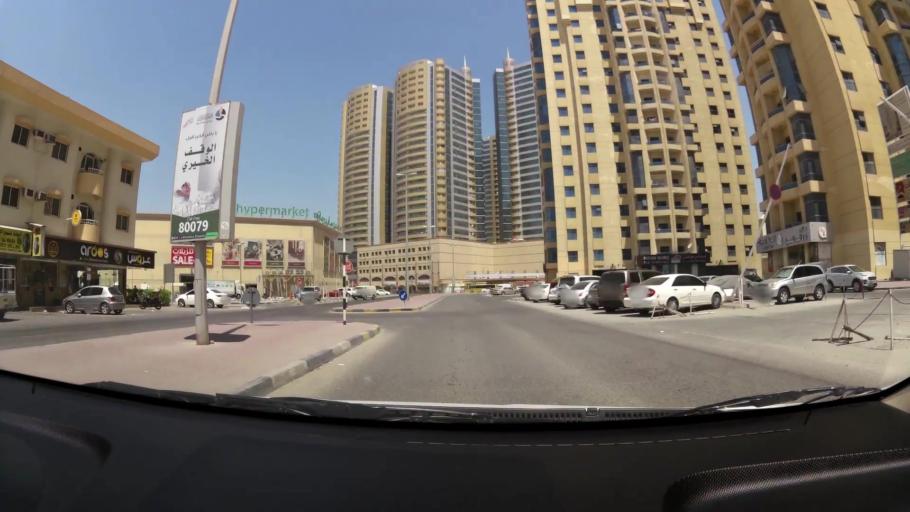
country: AE
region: Ajman
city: Ajman
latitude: 25.3934
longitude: 55.4571
